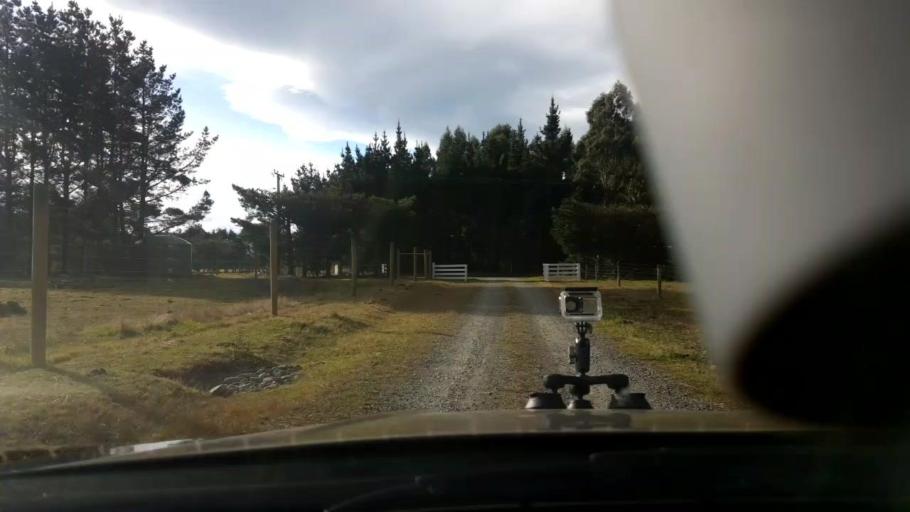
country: NZ
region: Canterbury
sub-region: Waimakariri District
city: Oxford
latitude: -43.3993
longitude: 172.3129
